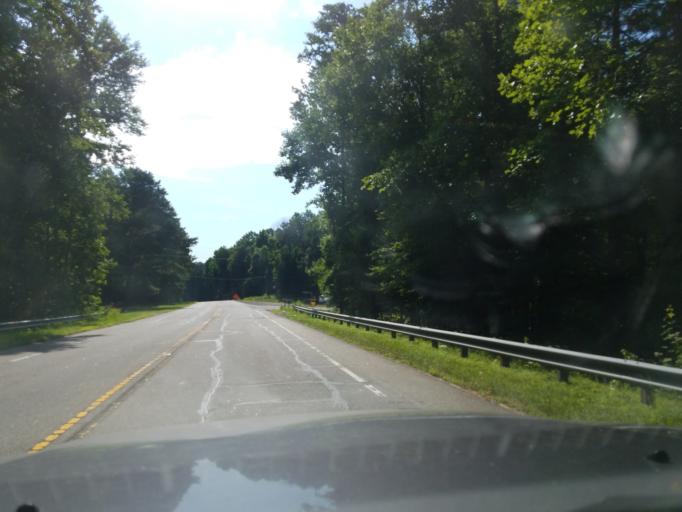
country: US
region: North Carolina
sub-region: Granville County
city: Oxford
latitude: 36.3139
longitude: -78.5383
